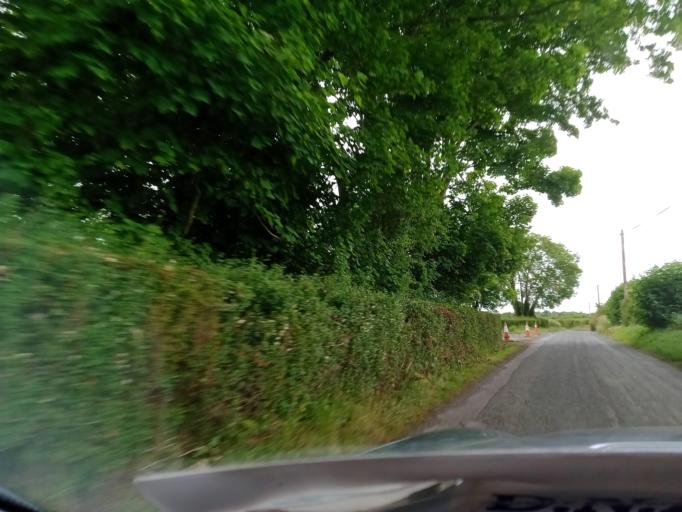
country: IE
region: Leinster
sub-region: Kilkenny
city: Thomastown
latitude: 52.5633
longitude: -7.1979
